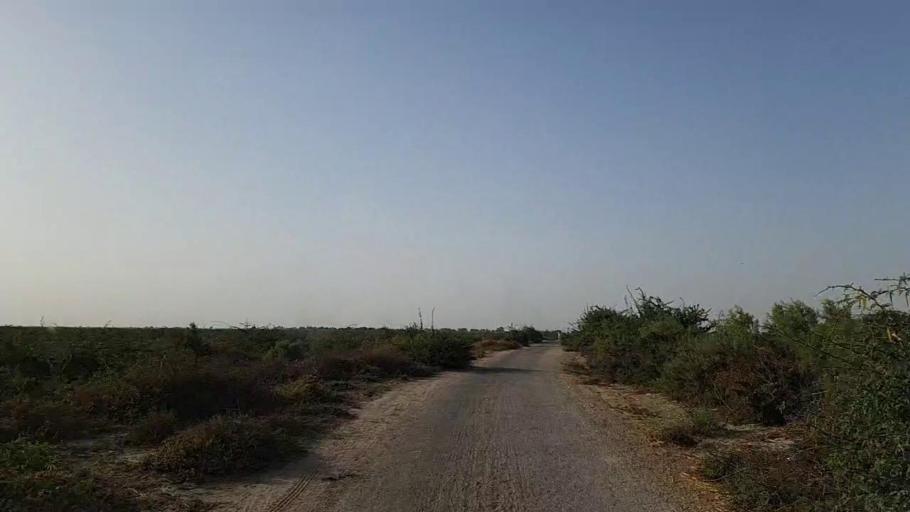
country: PK
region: Sindh
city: Jati
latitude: 24.3046
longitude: 68.1673
